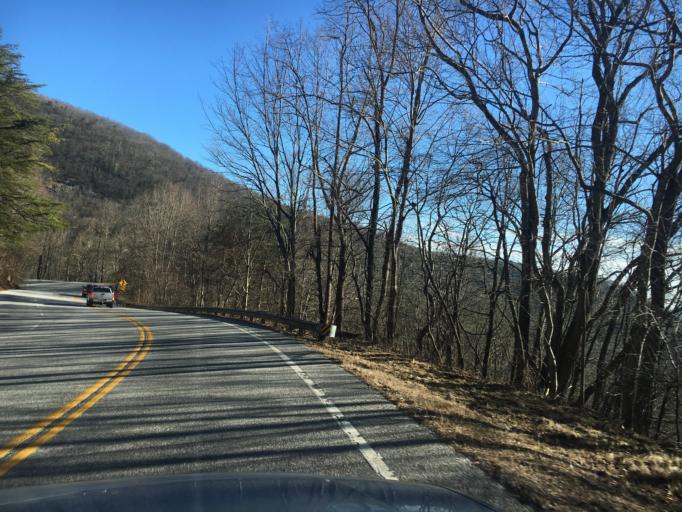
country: US
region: Georgia
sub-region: Union County
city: Blairsville
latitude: 34.7201
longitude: -83.9120
